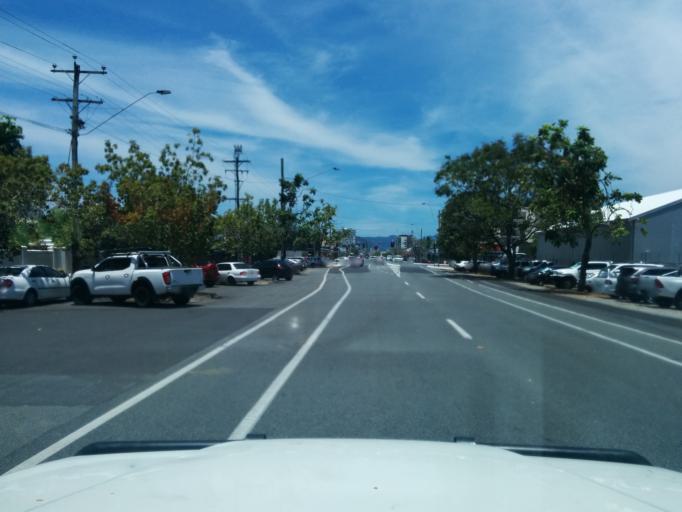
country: AU
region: Queensland
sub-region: Cairns
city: Cairns
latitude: -16.9168
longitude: 145.7663
